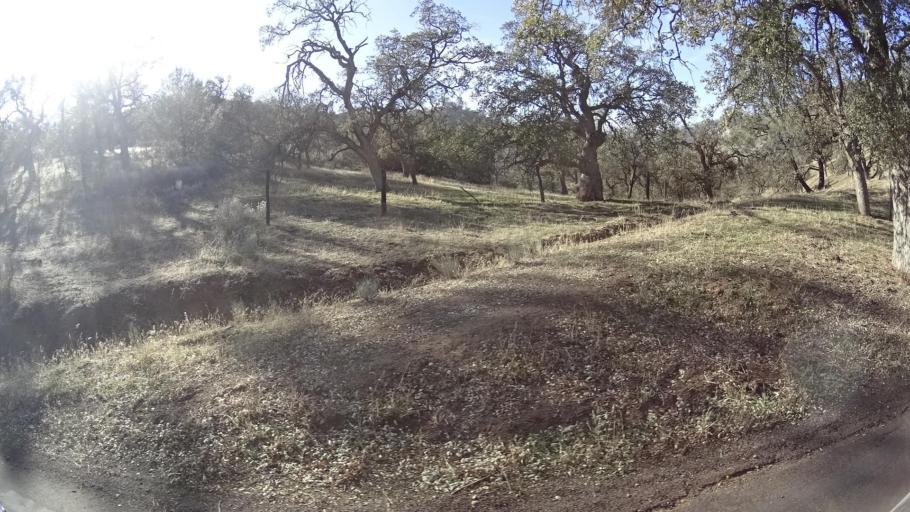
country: US
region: California
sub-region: Kern County
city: Bodfish
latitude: 35.3754
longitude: -118.5596
